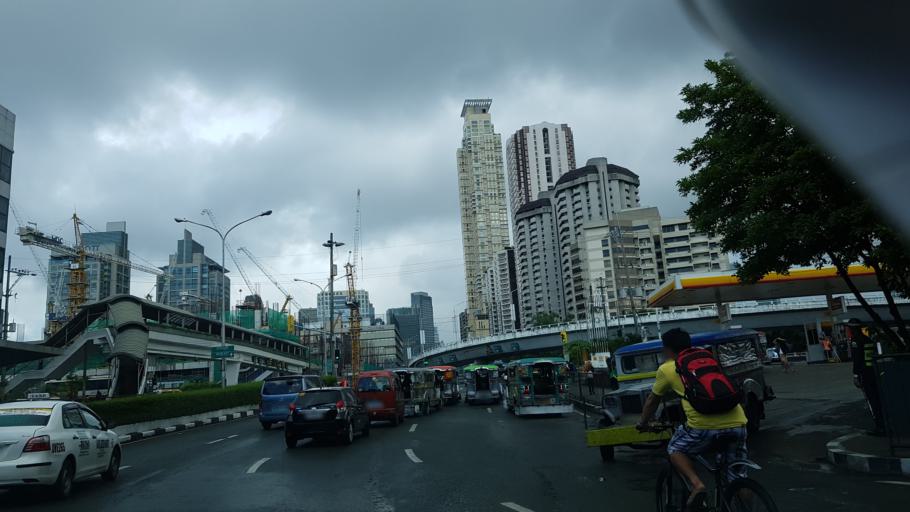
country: PH
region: Metro Manila
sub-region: Makati City
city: Makati City
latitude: 14.5496
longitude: 121.0301
